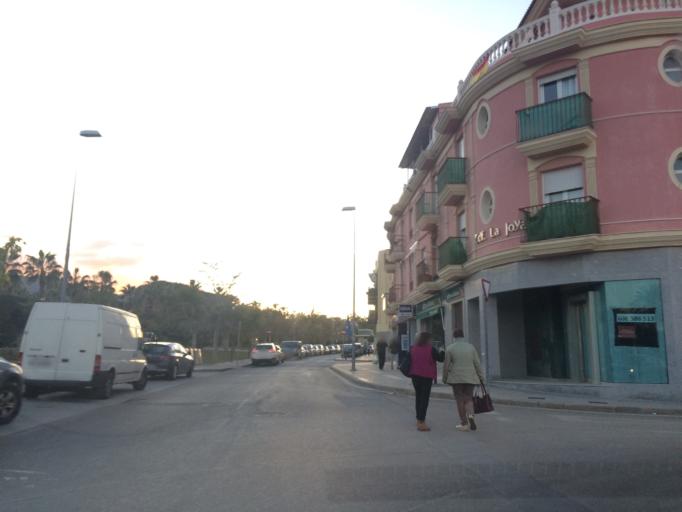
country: ES
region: Andalusia
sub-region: Provincia de Malaga
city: Alhaurin de la Torre
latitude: 36.6606
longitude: -4.5590
